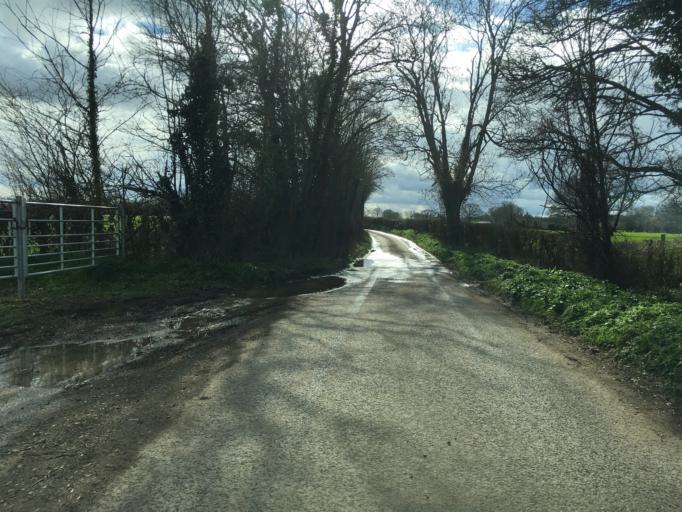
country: GB
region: England
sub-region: Gloucestershire
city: Newent
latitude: 51.8610
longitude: -2.3807
